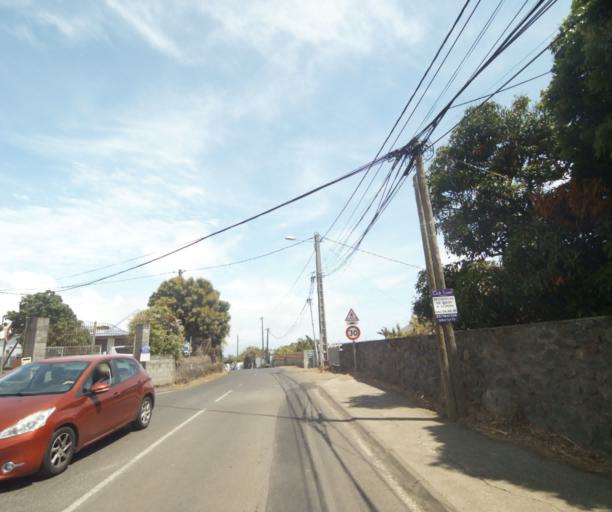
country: RE
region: Reunion
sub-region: Reunion
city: Trois-Bassins
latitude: -21.0848
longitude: 55.2718
